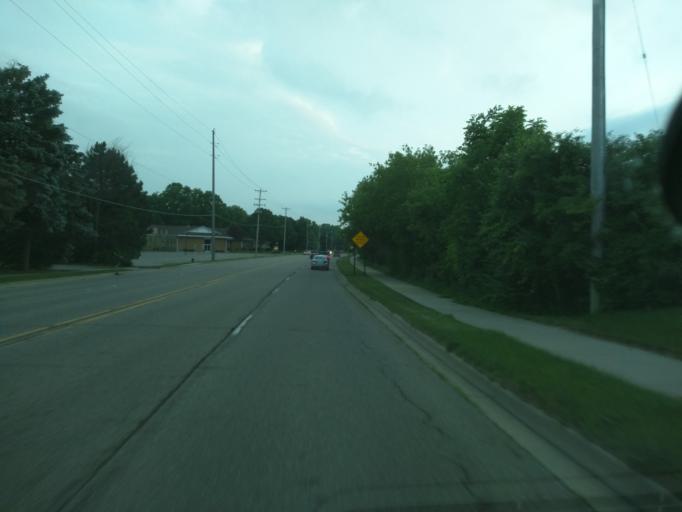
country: US
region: Michigan
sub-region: Ingham County
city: Okemos
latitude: 42.7185
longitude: -84.4231
